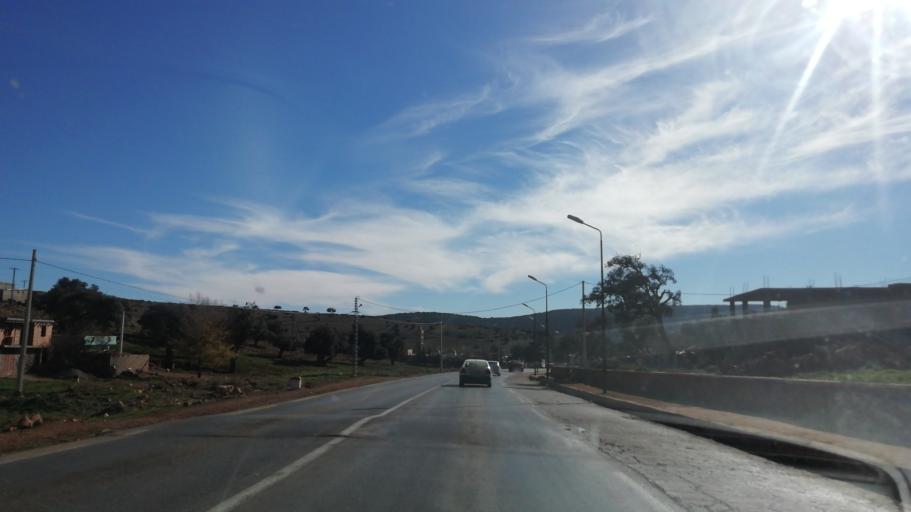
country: DZ
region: Tlemcen
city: Sebdou
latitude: 34.7283
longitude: -1.3372
